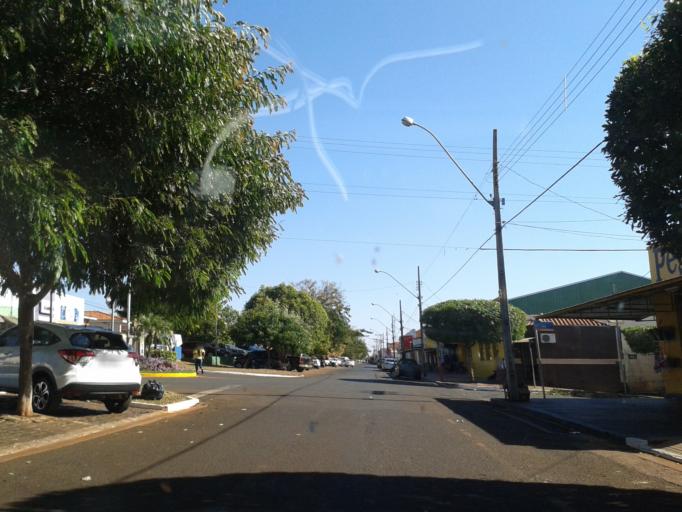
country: BR
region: Minas Gerais
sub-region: Santa Vitoria
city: Santa Vitoria
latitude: -18.8393
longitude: -50.1245
